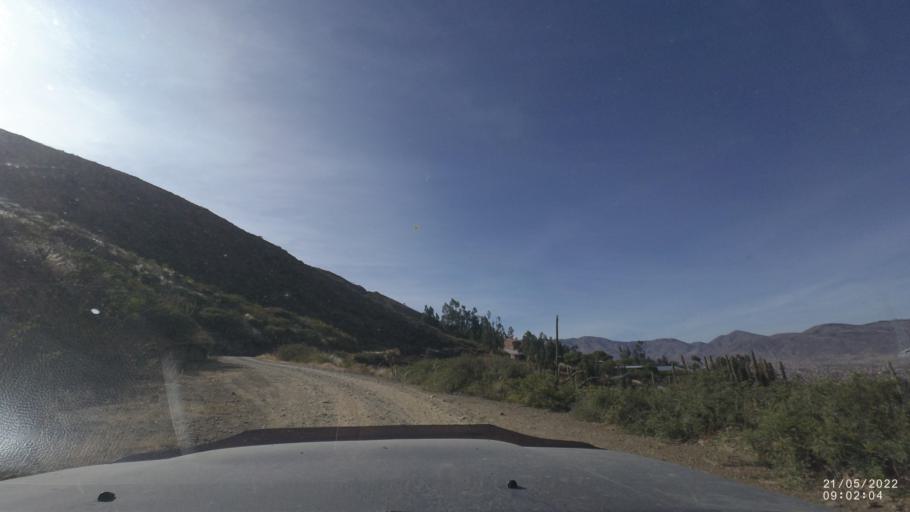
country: BO
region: Cochabamba
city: Cochabamba
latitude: -17.3762
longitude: -66.0321
